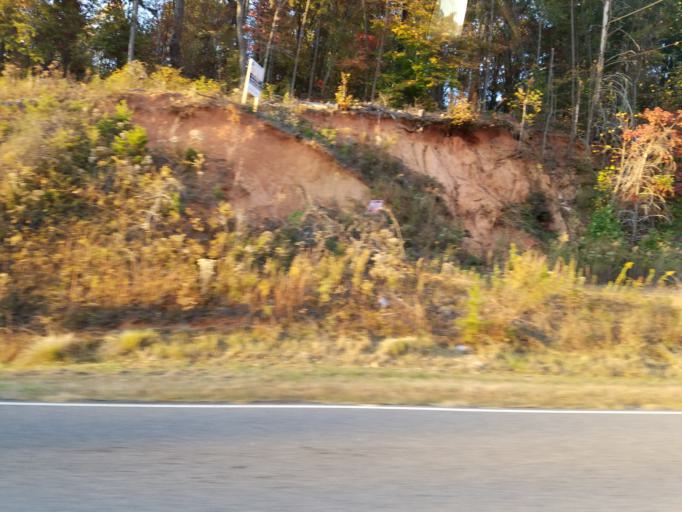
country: US
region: Georgia
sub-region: Lumpkin County
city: Dahlonega
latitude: 34.5274
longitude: -83.9962
